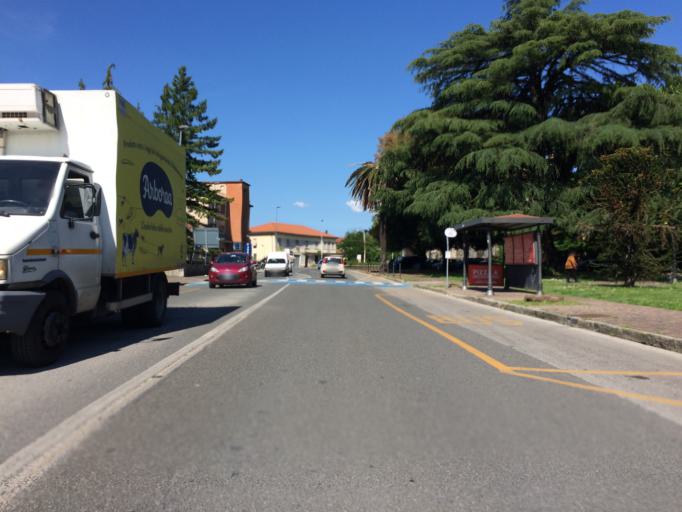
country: IT
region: Liguria
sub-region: Provincia di La Spezia
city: Sarzana
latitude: 44.1102
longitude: 9.9648
